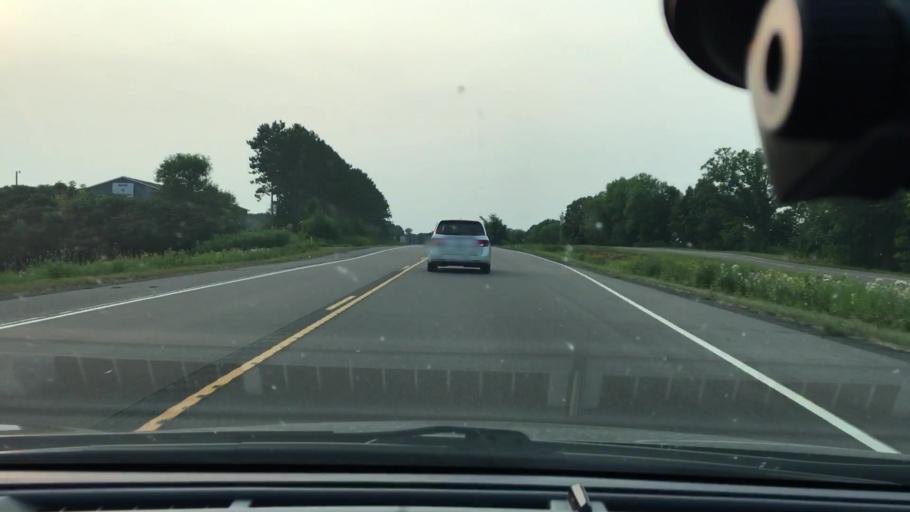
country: US
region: Minnesota
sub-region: Mille Lacs County
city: Vineland
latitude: 46.1377
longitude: -93.6985
